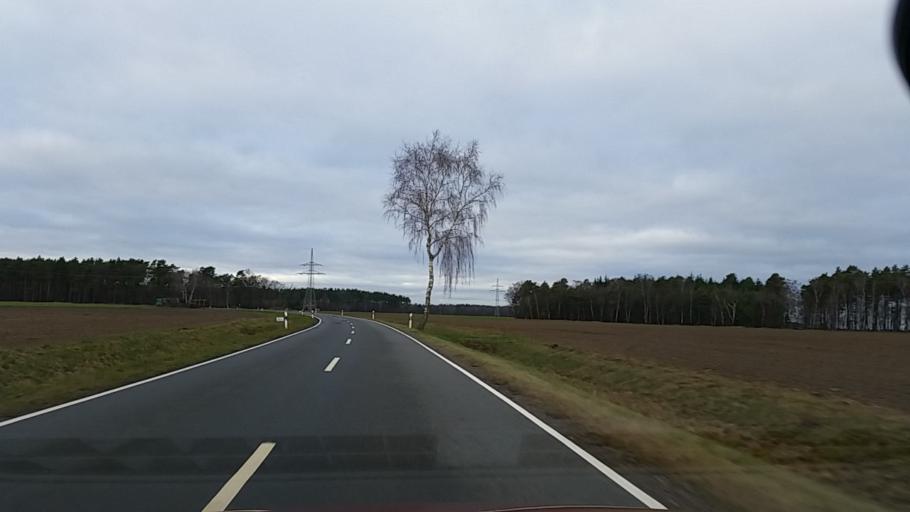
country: DE
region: Lower Saxony
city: Wittingen
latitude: 52.6805
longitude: 10.7922
